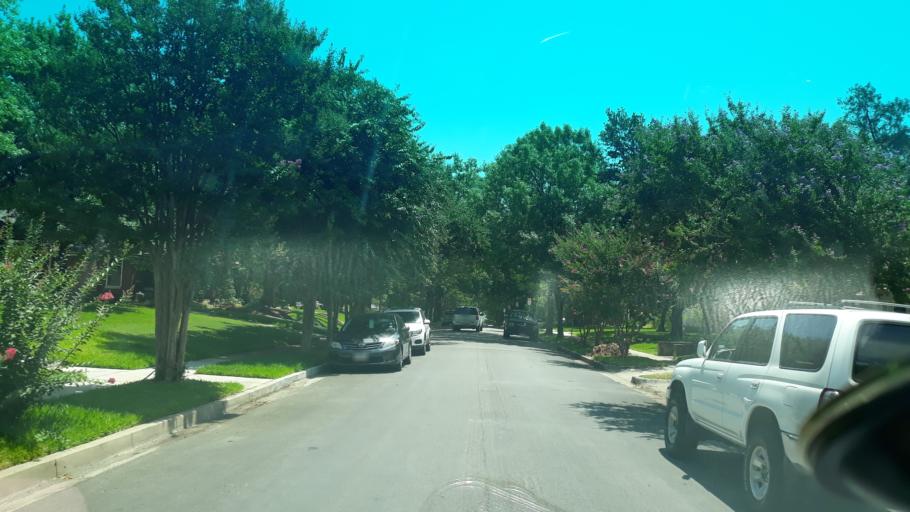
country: US
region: Texas
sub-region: Dallas County
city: Highland Park
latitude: 32.8136
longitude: -96.7371
